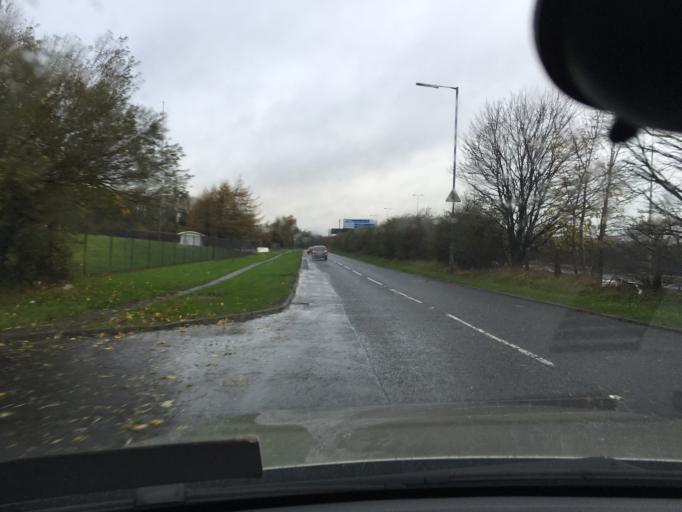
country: GB
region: Northern Ireland
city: Carnmoney
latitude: 54.6693
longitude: -5.9652
